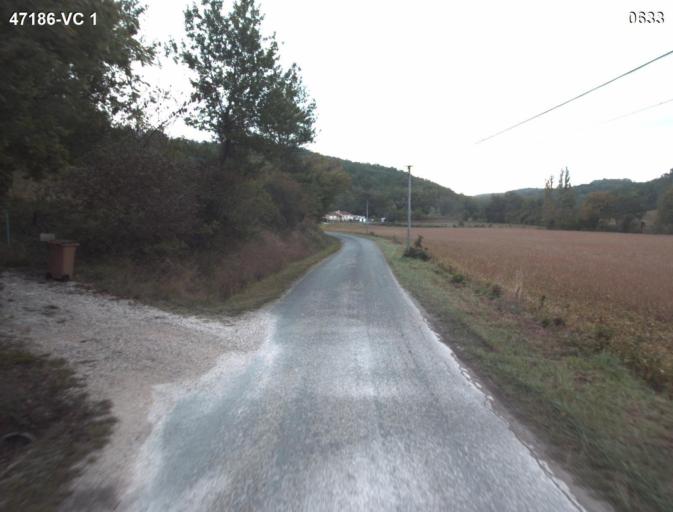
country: FR
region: Aquitaine
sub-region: Departement du Lot-et-Garonne
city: Sainte-Colombe-en-Bruilhois
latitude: 44.1937
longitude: 0.4415
